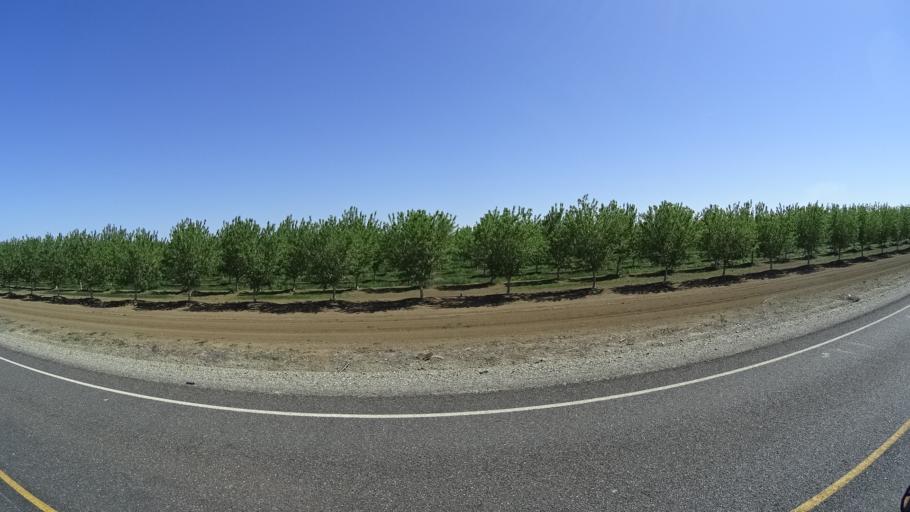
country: US
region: California
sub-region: Glenn County
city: Willows
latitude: 39.5815
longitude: -122.2497
